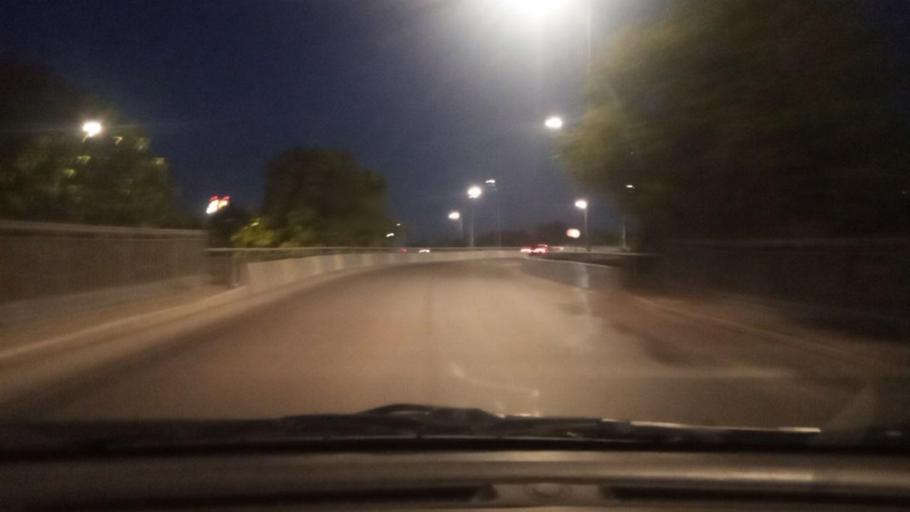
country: UZ
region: Toshkent Shahri
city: Tashkent
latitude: 41.2673
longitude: 69.2645
